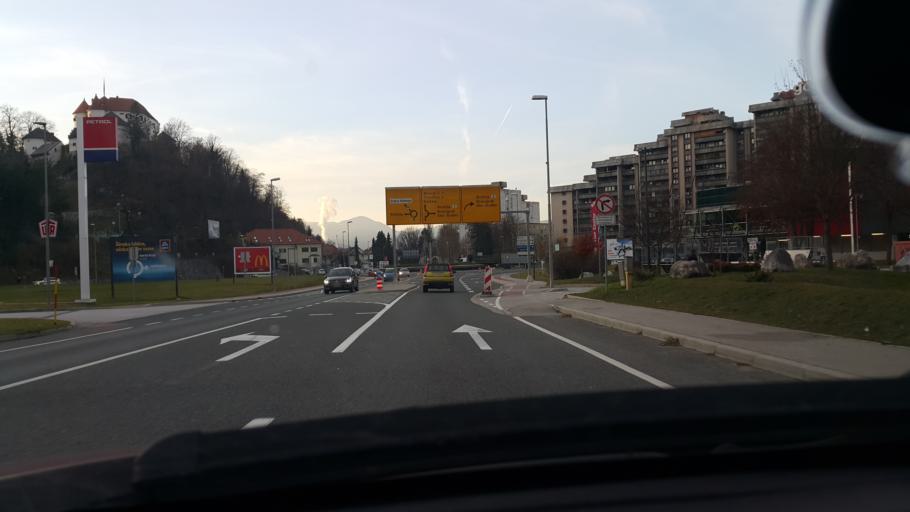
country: SI
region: Velenje
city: Velenje
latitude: 46.3565
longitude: 15.1147
